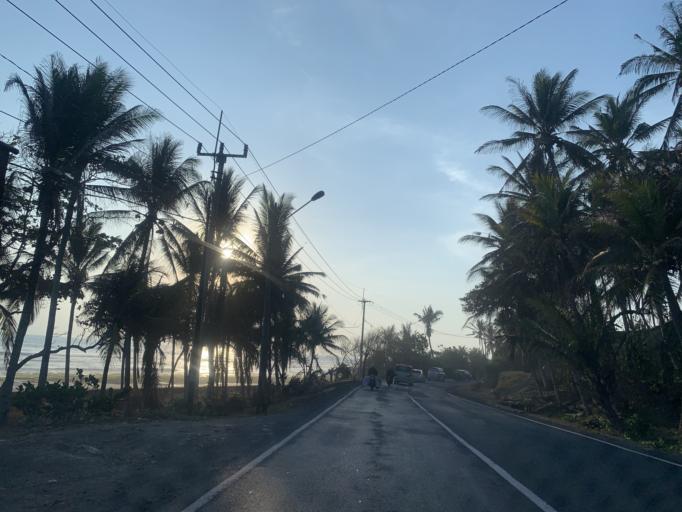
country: ID
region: Bali
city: Banjar Swastika
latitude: -8.4631
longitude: 114.9104
